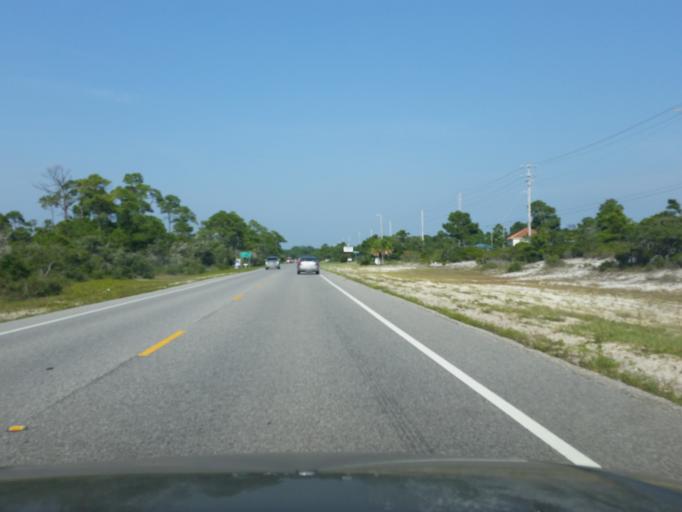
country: US
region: Alabama
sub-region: Mobile County
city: Dauphin Island
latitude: 30.2377
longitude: -87.9061
